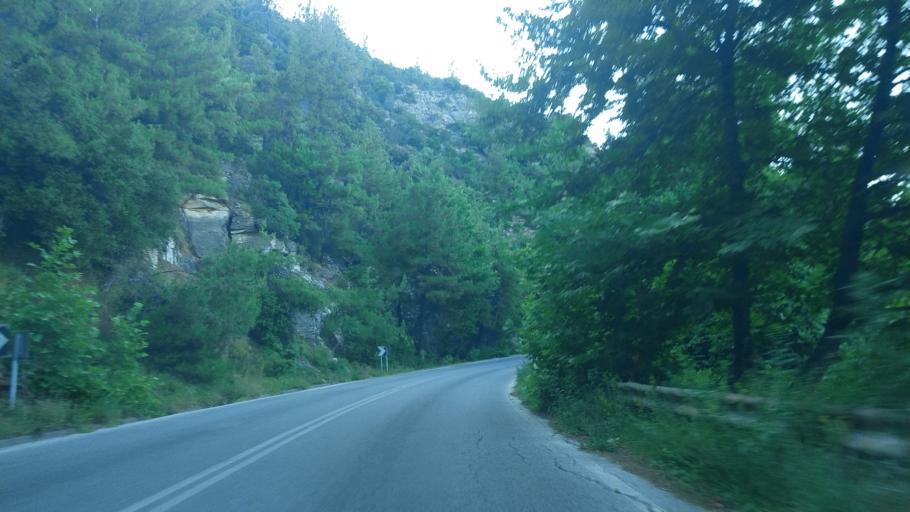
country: GR
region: East Macedonia and Thrace
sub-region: Nomos Kavalas
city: Potamia
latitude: 40.7249
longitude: 24.7324
